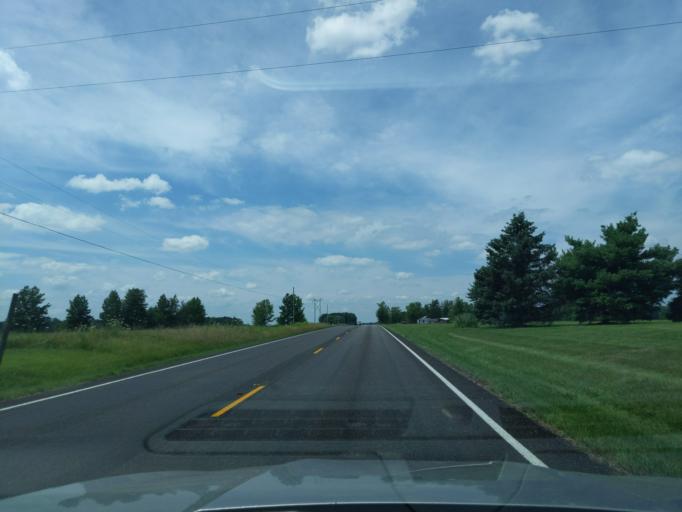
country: US
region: Indiana
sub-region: Ripley County
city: Osgood
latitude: 39.2451
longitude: -85.3498
